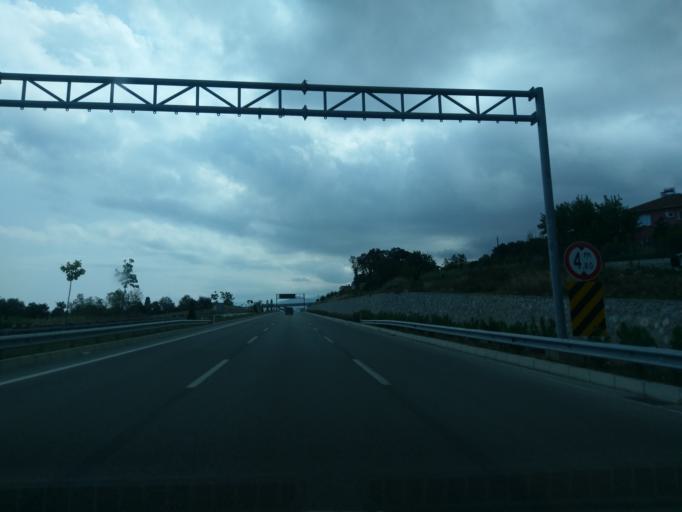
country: TR
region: Sinop
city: Gerze
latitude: 41.7980
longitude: 35.1825
